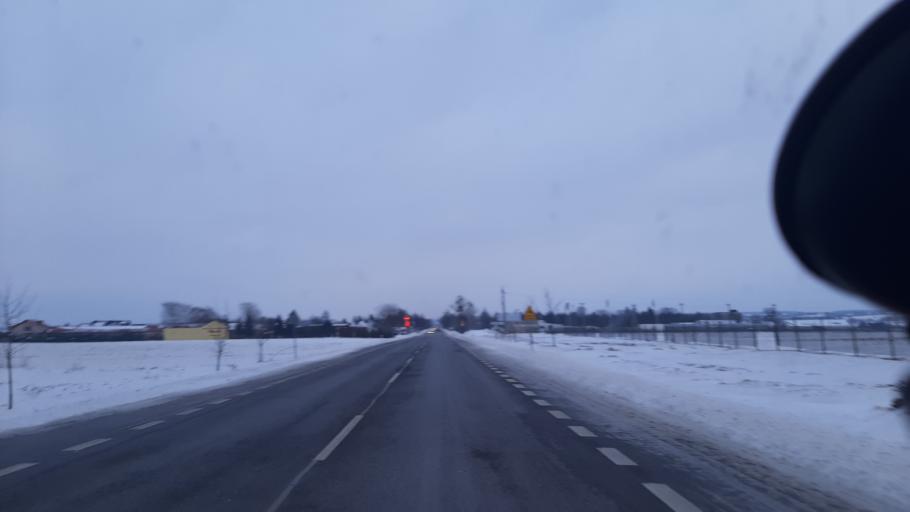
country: PL
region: Lublin Voivodeship
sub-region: Powiat pulawski
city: Markuszow
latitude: 51.3789
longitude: 22.2411
